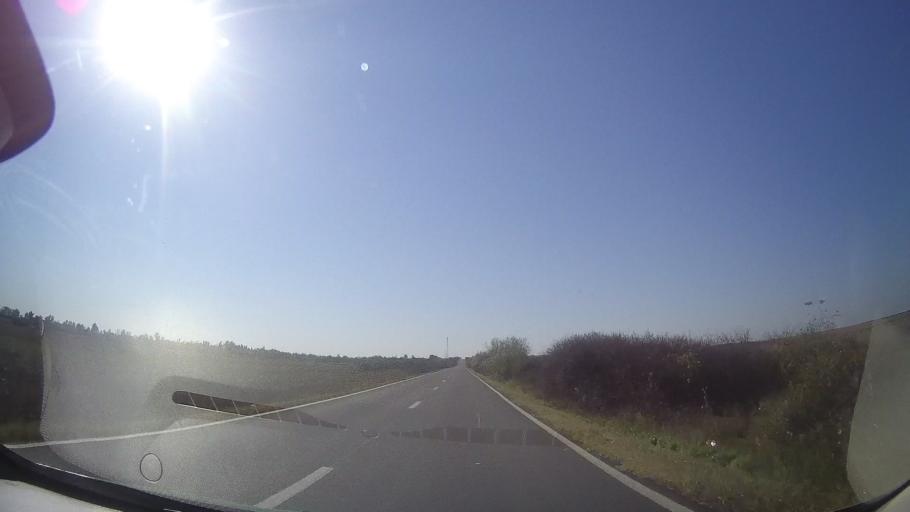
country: RO
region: Timis
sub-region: Comuna Belint
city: Belint
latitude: 45.7731
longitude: 21.7304
